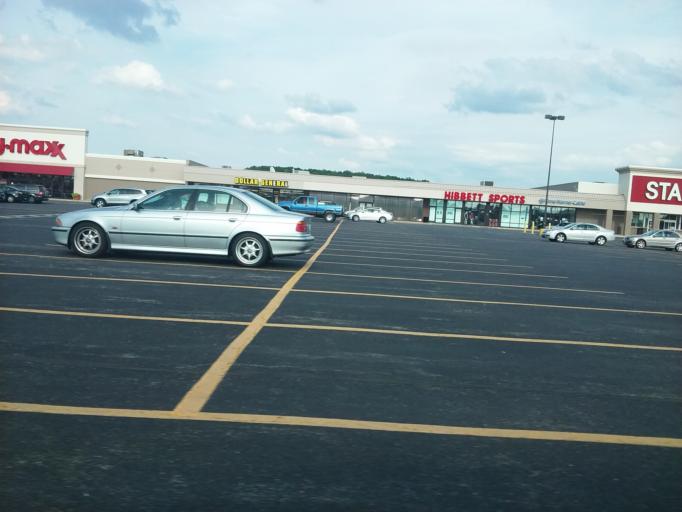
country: US
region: Ohio
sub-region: Wood County
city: Bowling Green
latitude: 41.3551
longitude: -83.6494
